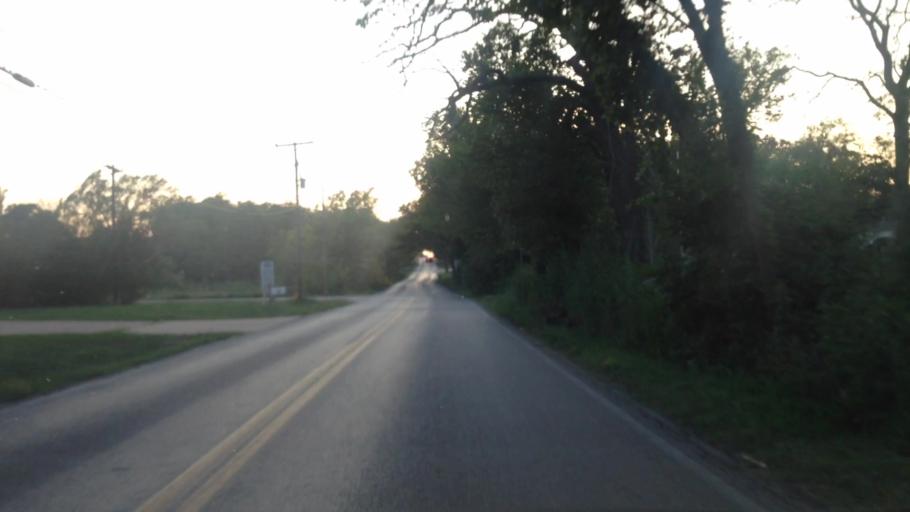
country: US
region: Texas
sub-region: Tarrant County
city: Kennedale
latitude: 32.6332
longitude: -97.1939
